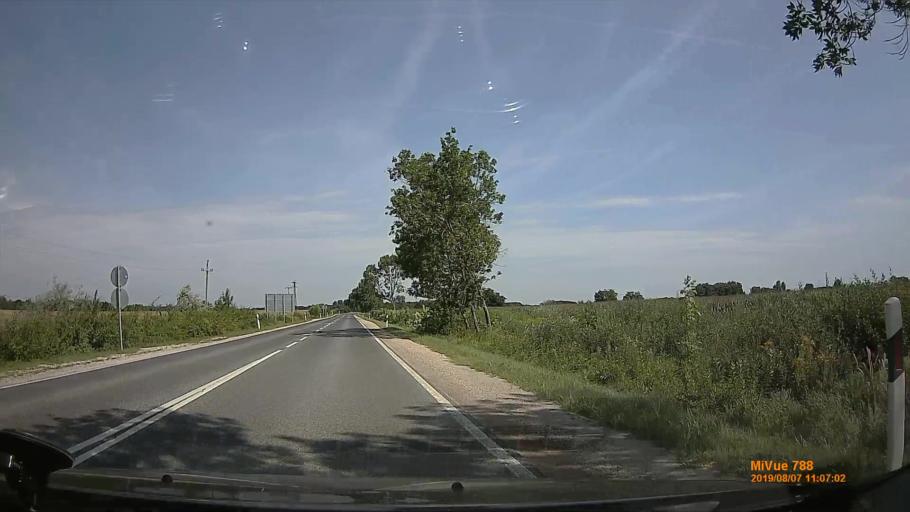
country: SI
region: Lendava-Lendva
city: Lendava
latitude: 46.6197
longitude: 16.4653
